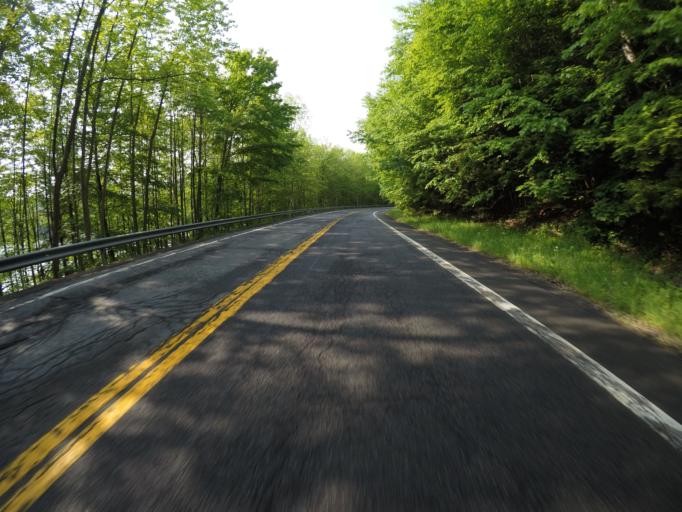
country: US
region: New York
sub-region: Sullivan County
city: Livingston Manor
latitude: 42.0910
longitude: -74.7989
